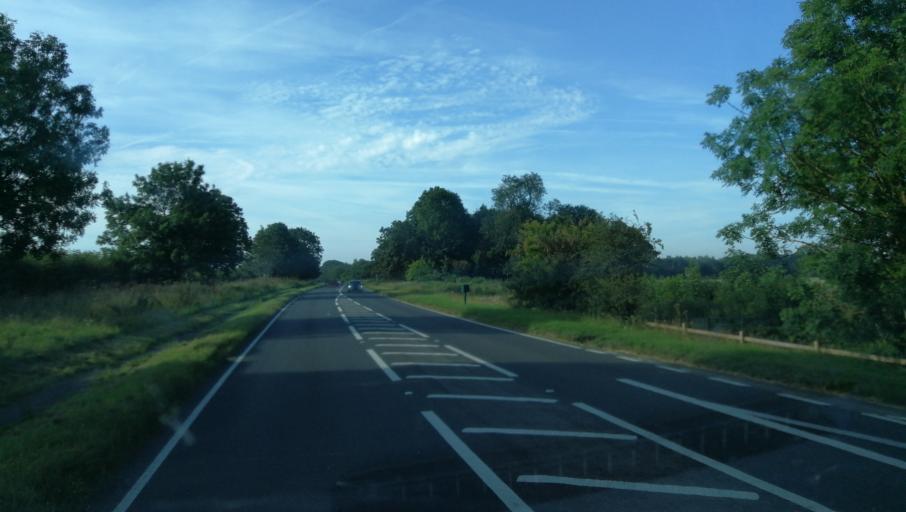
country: GB
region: England
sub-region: Oxfordshire
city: Deddington
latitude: 51.9884
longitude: -1.3217
